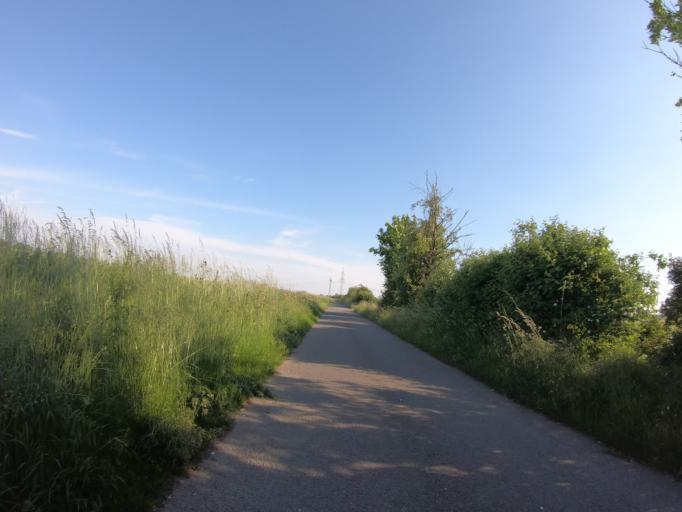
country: DE
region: Lower Saxony
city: Meine
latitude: 52.3764
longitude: 10.5429
